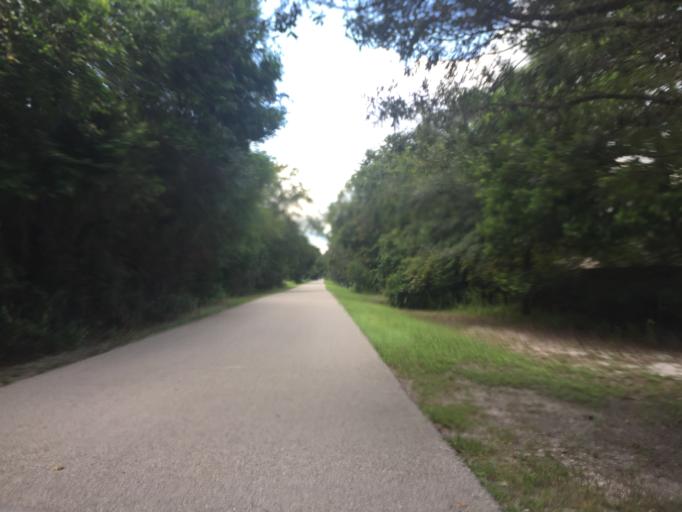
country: US
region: Florida
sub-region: Seminole County
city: Oviedo
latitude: 28.6775
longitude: -81.2157
